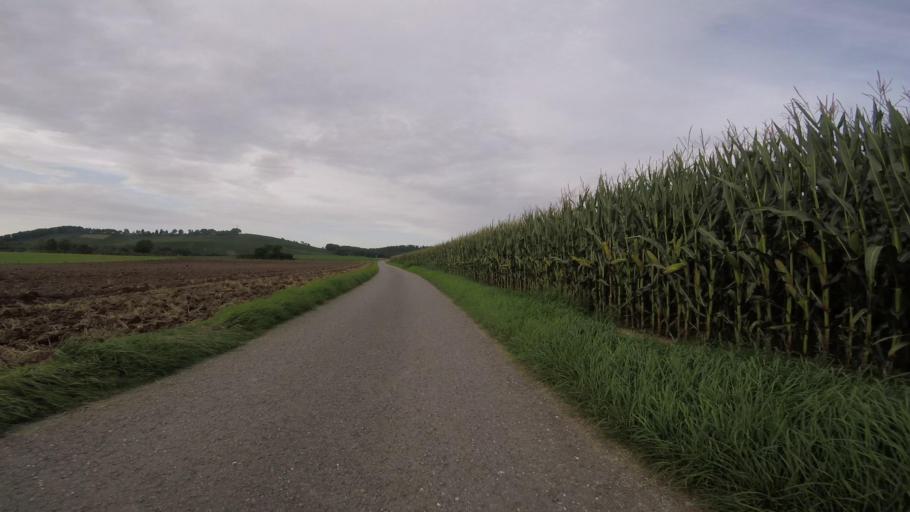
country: DE
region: Baden-Wuerttemberg
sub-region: Regierungsbezirk Stuttgart
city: Aspach
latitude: 48.9884
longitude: 9.3736
